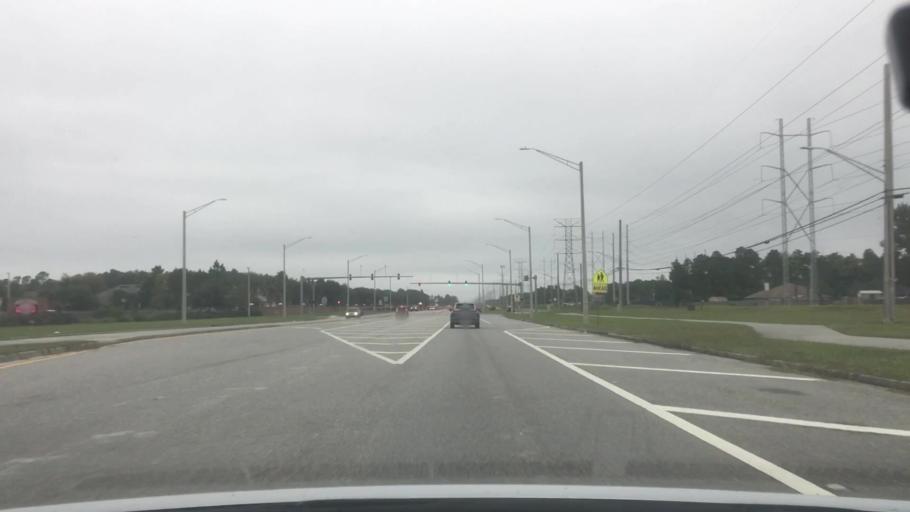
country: US
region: Florida
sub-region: Duval County
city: Atlantic Beach
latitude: 30.3329
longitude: -81.4896
